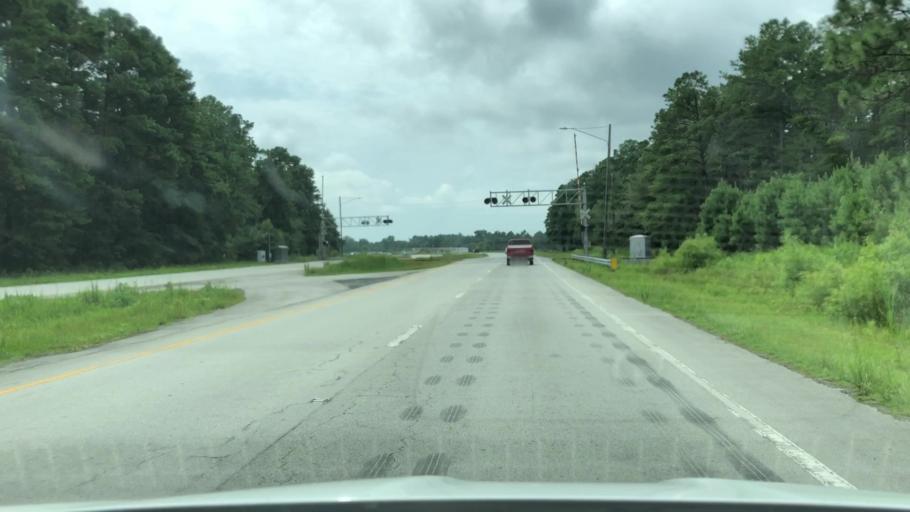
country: US
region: North Carolina
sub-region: Carteret County
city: Newport
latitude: 34.8168
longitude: -76.8787
